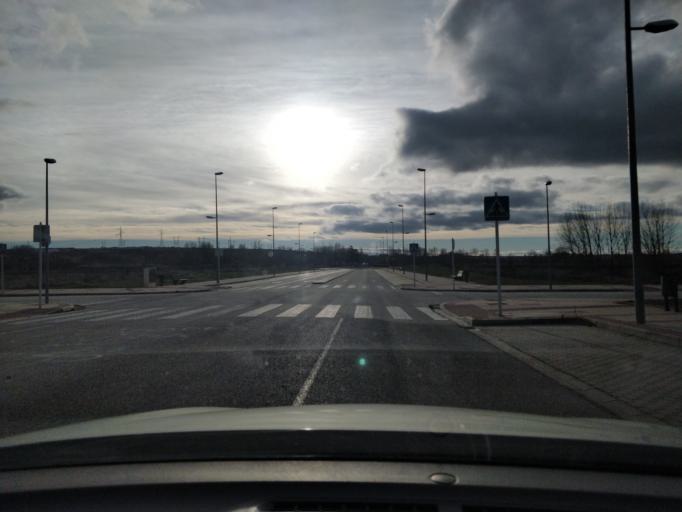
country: ES
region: Castille and Leon
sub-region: Provincia de Burgos
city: Villalbilla de Burgos
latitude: 42.3538
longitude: -3.7619
